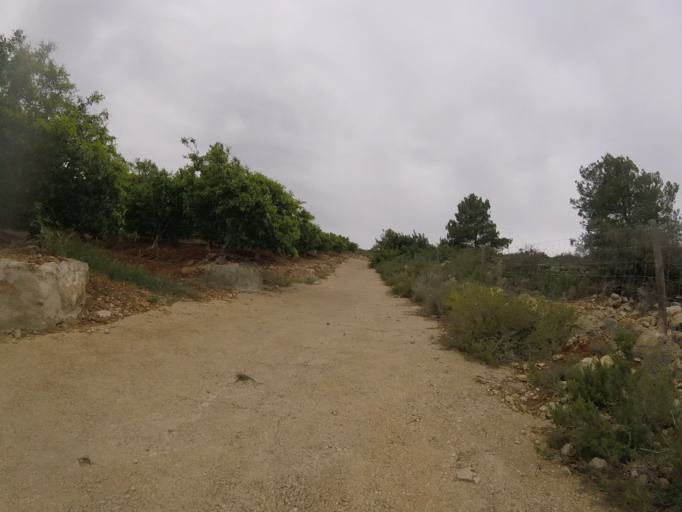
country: ES
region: Valencia
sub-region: Provincia de Castello
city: Alcala de Xivert
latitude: 40.2801
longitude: 0.2513
